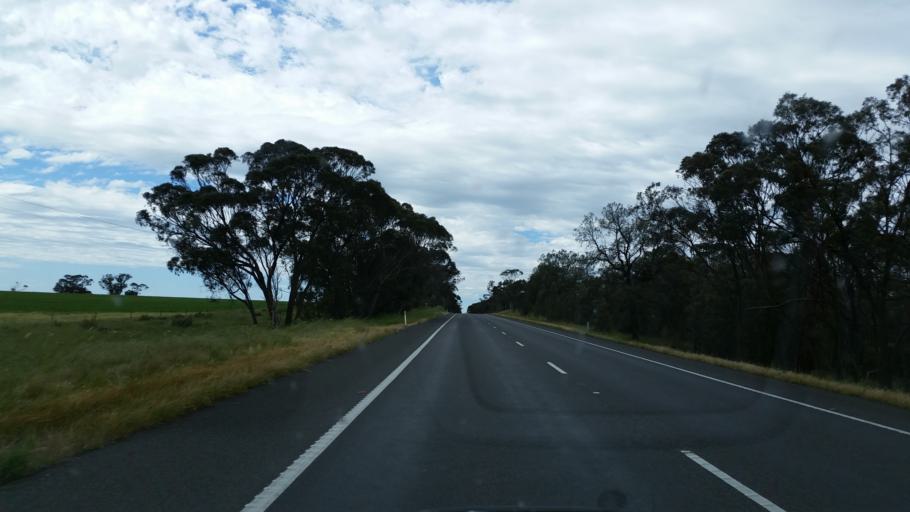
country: AU
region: South Australia
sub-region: Tatiara
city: Bordertown
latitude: -36.3482
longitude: 140.9979
